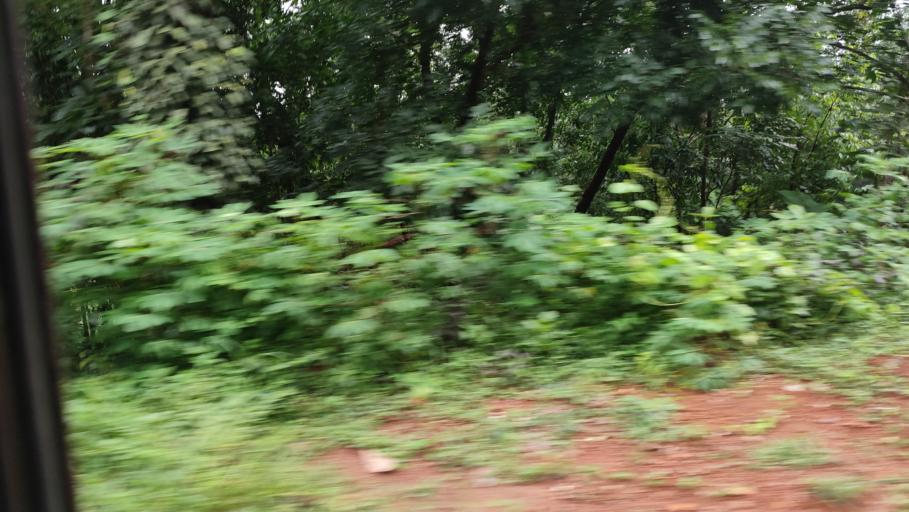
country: IN
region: Kerala
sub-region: Kasaragod District
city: Nileshwar
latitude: 12.2972
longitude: 75.2888
